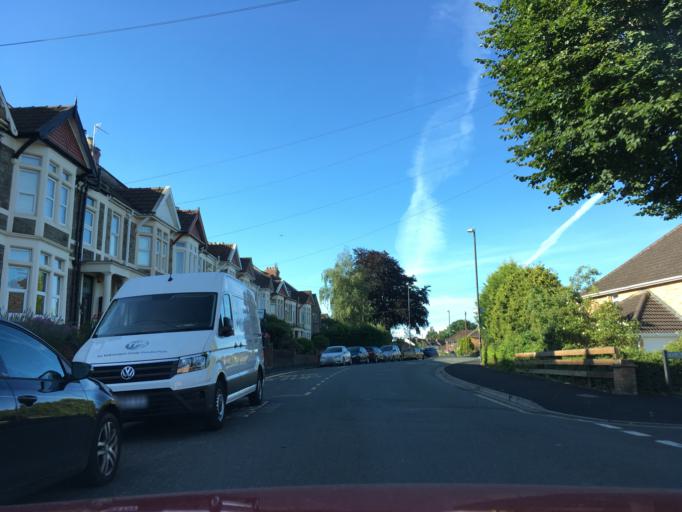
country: GB
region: England
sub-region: South Gloucestershire
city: Kingswood
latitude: 51.4451
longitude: -2.5487
